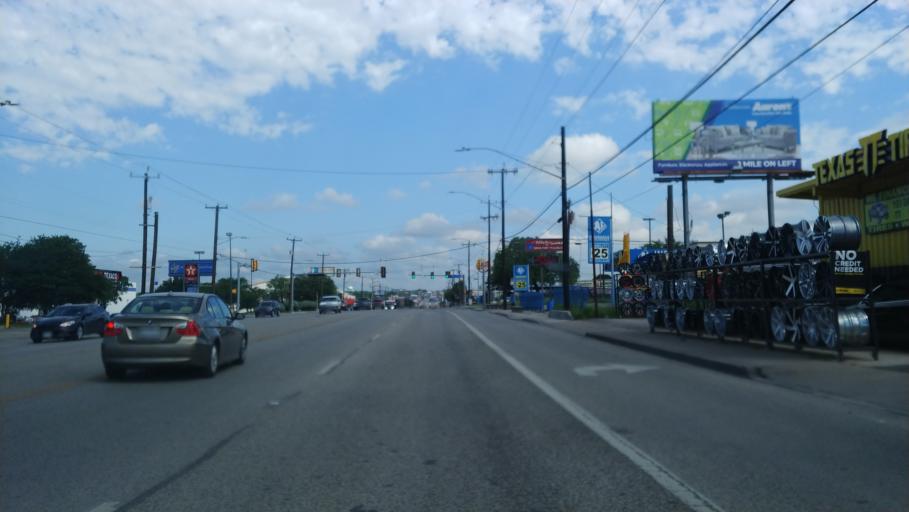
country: US
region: Texas
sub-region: Bexar County
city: Balcones Heights
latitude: 29.4727
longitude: -98.5341
